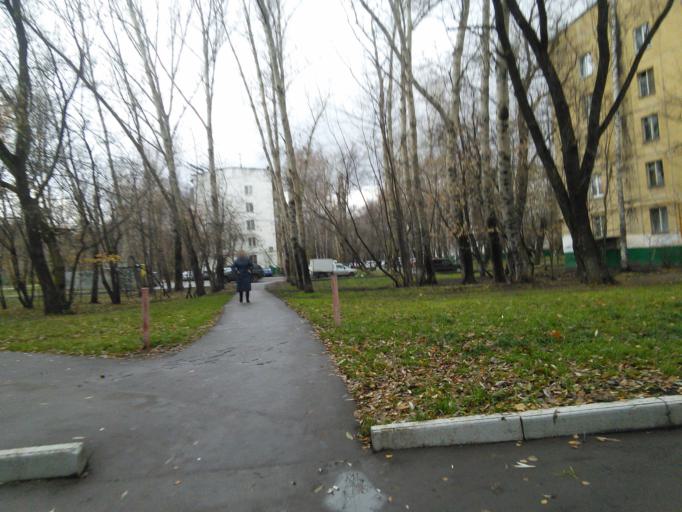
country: RU
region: Moscow
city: Tsaritsyno
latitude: 55.6321
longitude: 37.6540
